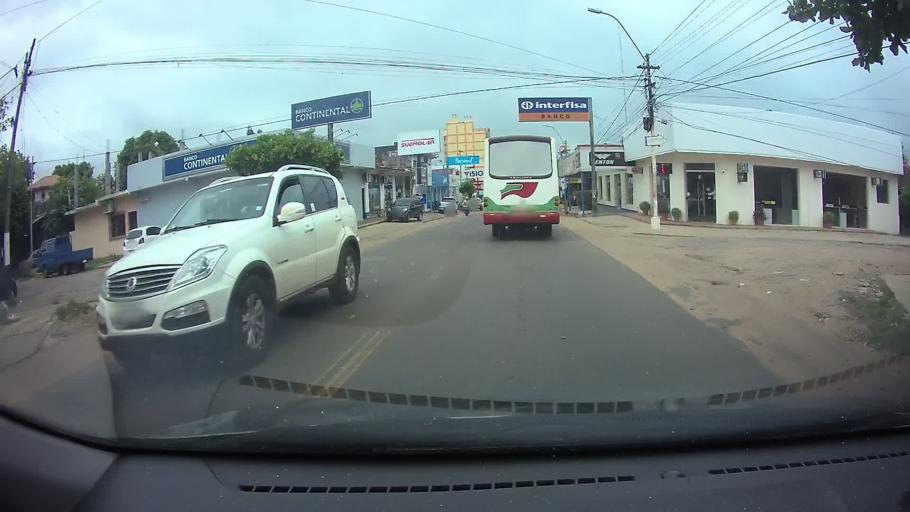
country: PY
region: Paraguari
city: Carapegua
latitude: -25.7679
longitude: -57.2401
